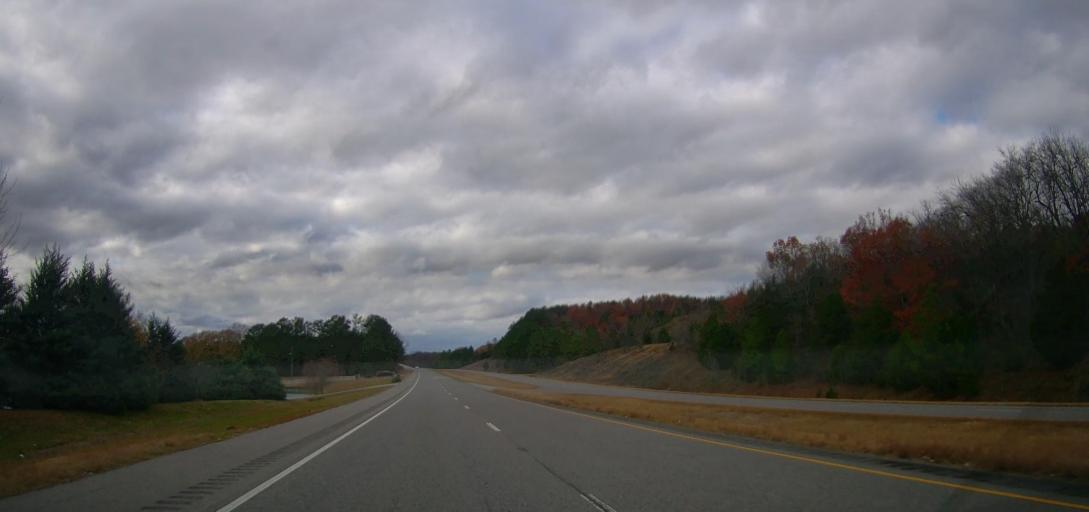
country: US
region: Alabama
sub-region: Lawrence County
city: Town Creek
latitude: 34.6248
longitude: -87.4742
